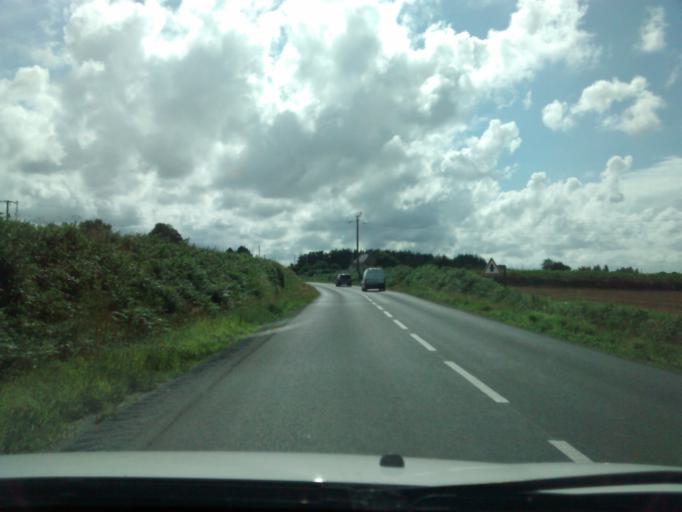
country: FR
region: Brittany
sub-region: Departement des Cotes-d'Armor
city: Plouguiel
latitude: 48.7928
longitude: -3.2635
